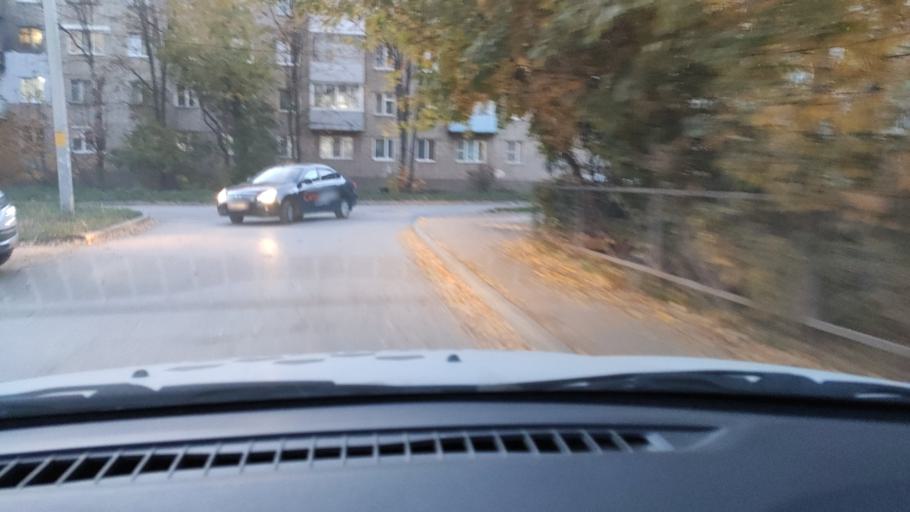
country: RU
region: Perm
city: Perm
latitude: 57.9639
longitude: 56.2330
